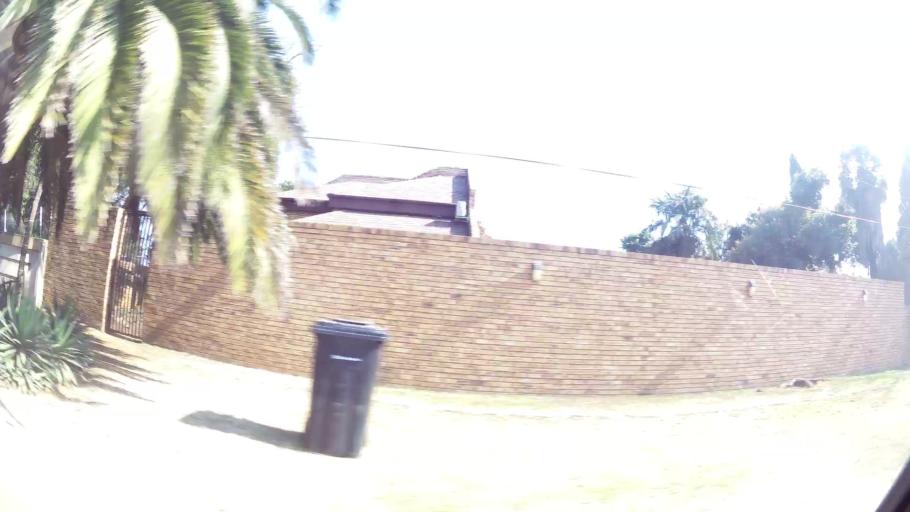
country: ZA
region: Gauteng
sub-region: Ekurhuleni Metropolitan Municipality
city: Boksburg
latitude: -26.1873
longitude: 28.2849
